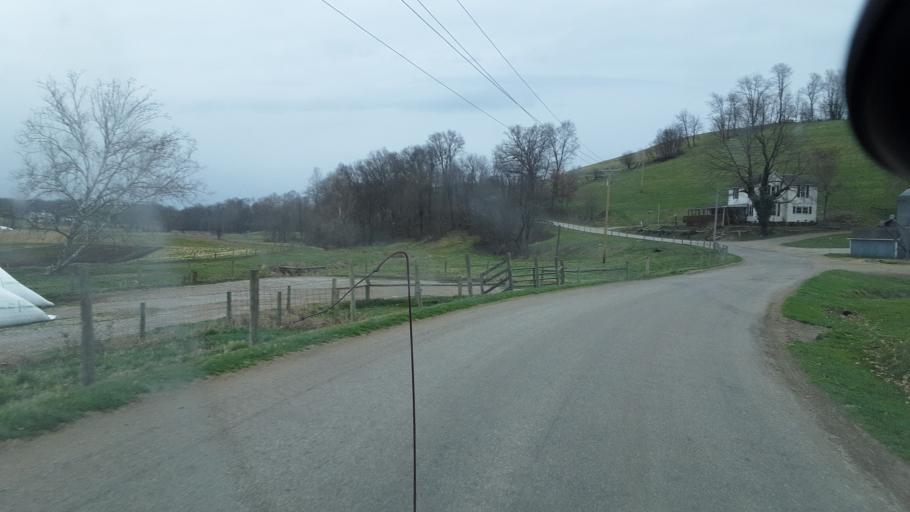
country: US
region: Ohio
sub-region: Coshocton County
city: West Lafayette
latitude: 40.3229
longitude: -81.6922
